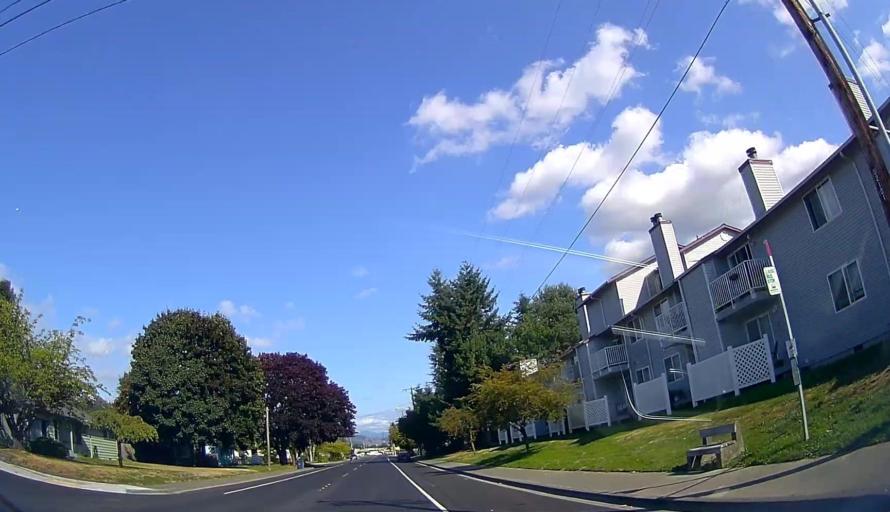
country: US
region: Washington
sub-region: Skagit County
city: Burlington
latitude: 48.4753
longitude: -122.3391
